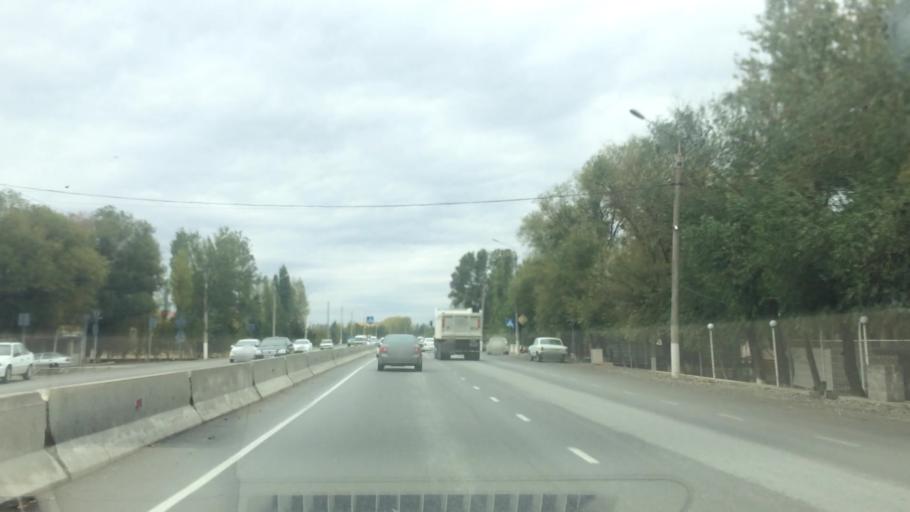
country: UZ
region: Jizzax
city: Jizzax
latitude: 39.9935
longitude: 67.5852
